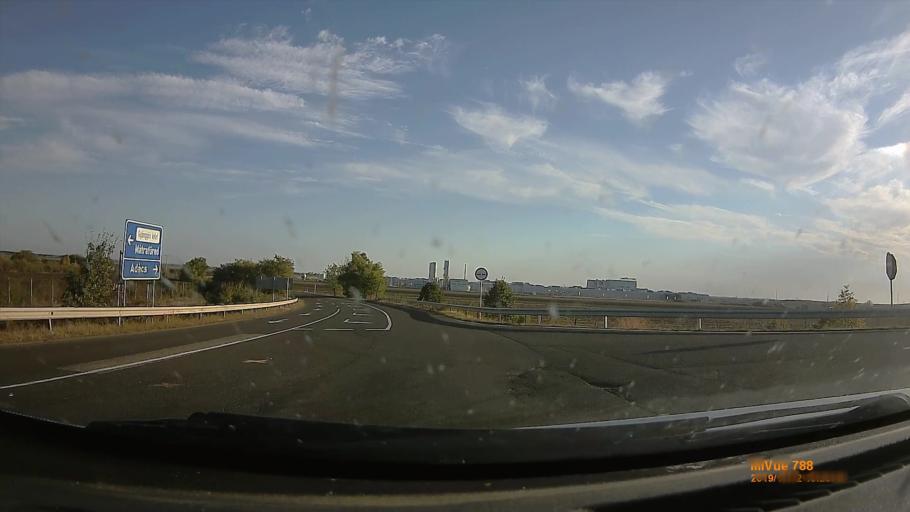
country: HU
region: Heves
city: Gyongyoshalasz
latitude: 47.7308
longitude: 19.9589
